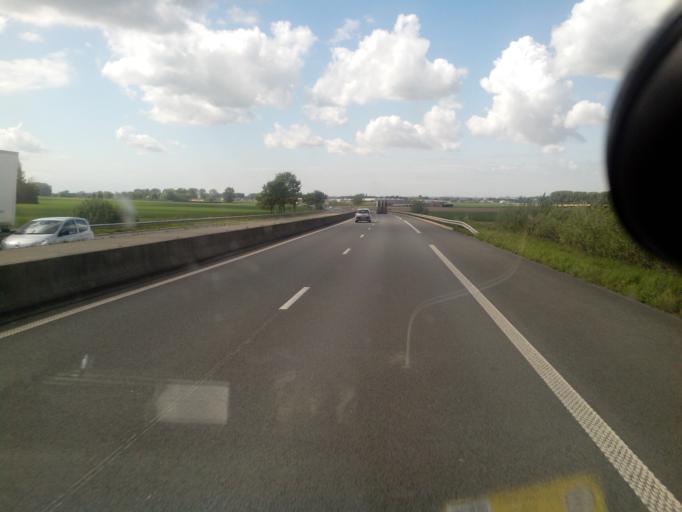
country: FR
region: Nord-Pas-de-Calais
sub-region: Departement du Nord
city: Quaedypre
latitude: 50.9394
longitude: 2.4602
